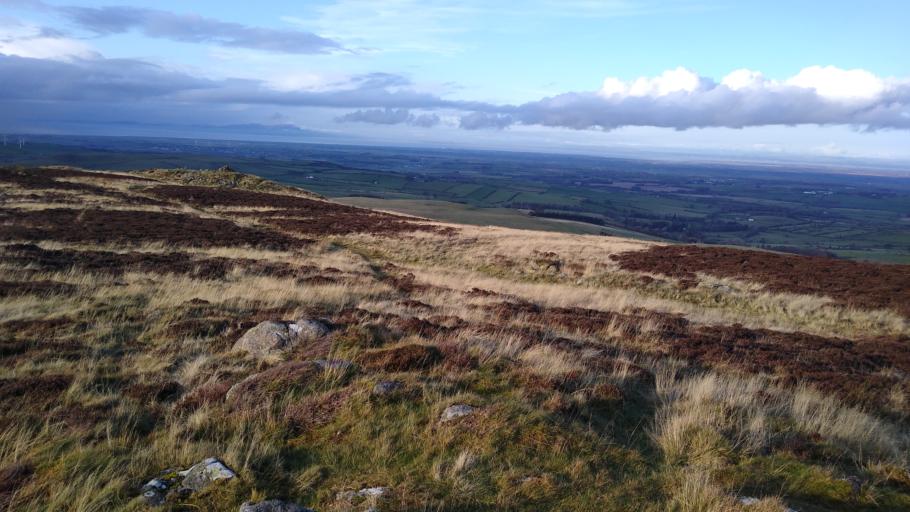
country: GB
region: England
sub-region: Cumbria
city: Wigton
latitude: 54.7088
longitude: -3.2044
